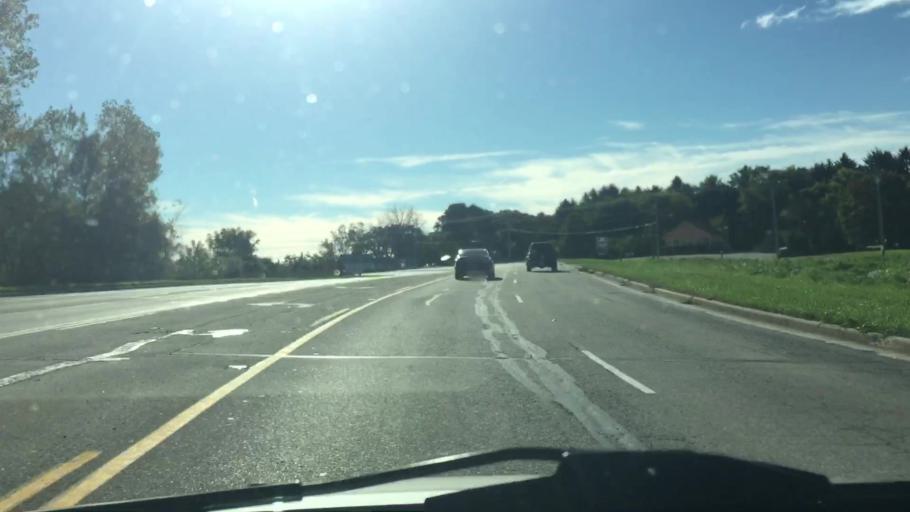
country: US
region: Wisconsin
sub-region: Waukesha County
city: Waukesha
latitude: 43.0413
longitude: -88.2235
